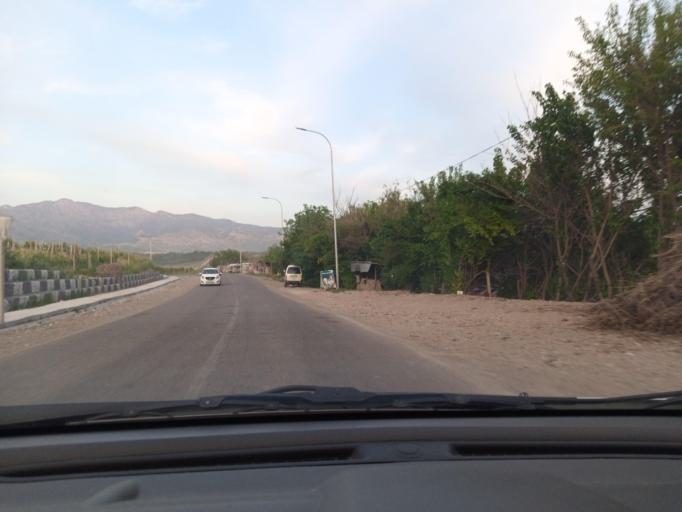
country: UZ
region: Toshkent
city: Parkent
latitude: 41.2457
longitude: 69.7341
